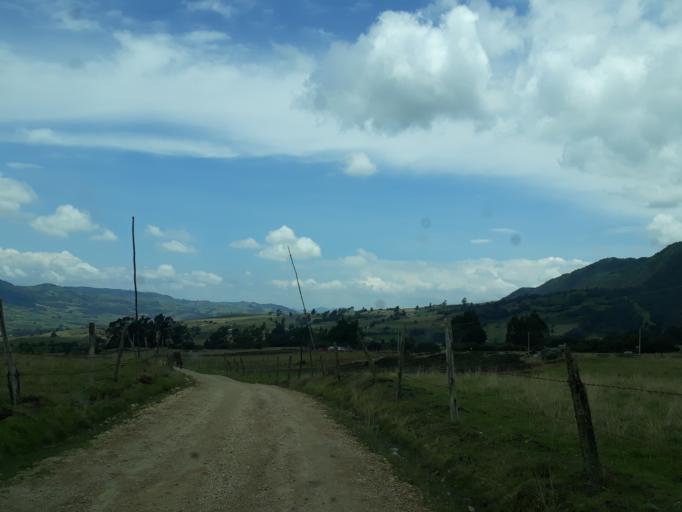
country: CO
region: Cundinamarca
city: Lenguazaque
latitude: 5.3173
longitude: -73.6267
